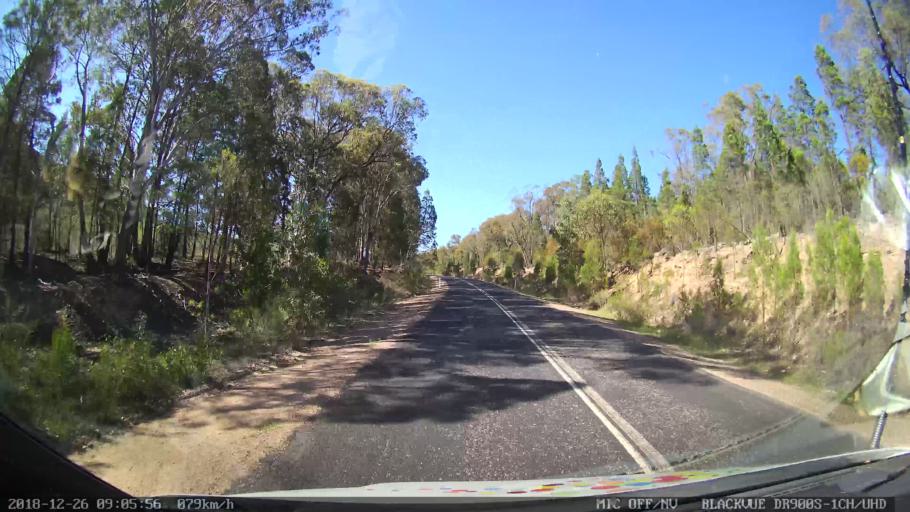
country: AU
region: New South Wales
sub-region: Mid-Western Regional
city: Kandos
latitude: -32.6882
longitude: 150.0048
